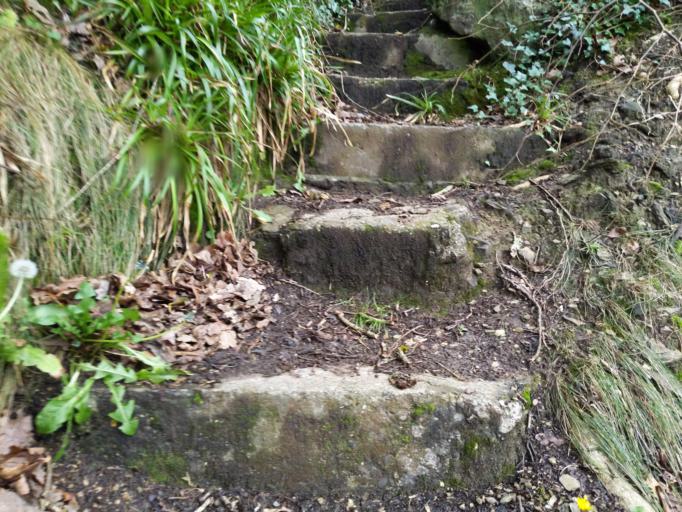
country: GB
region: England
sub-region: Cornwall
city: Fowey
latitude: 50.3326
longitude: -4.6280
